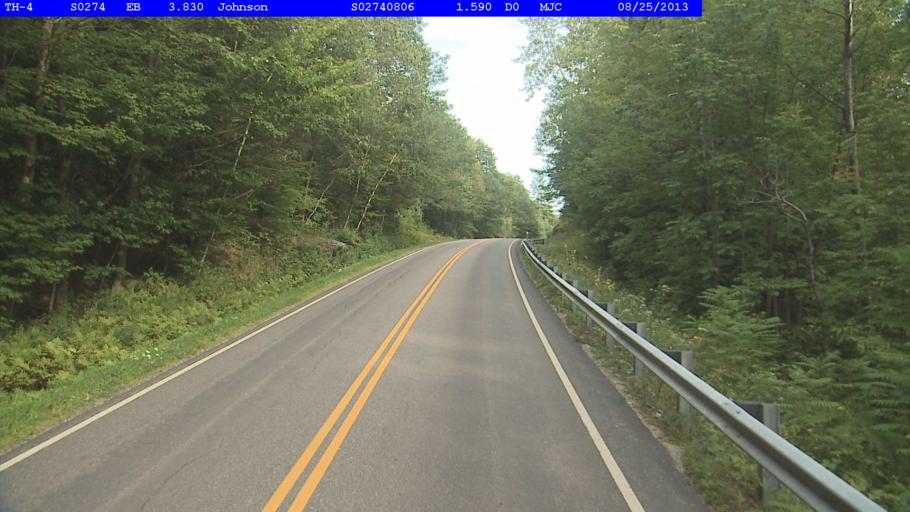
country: US
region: Vermont
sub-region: Lamoille County
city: Johnson
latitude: 44.6483
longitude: -72.7233
